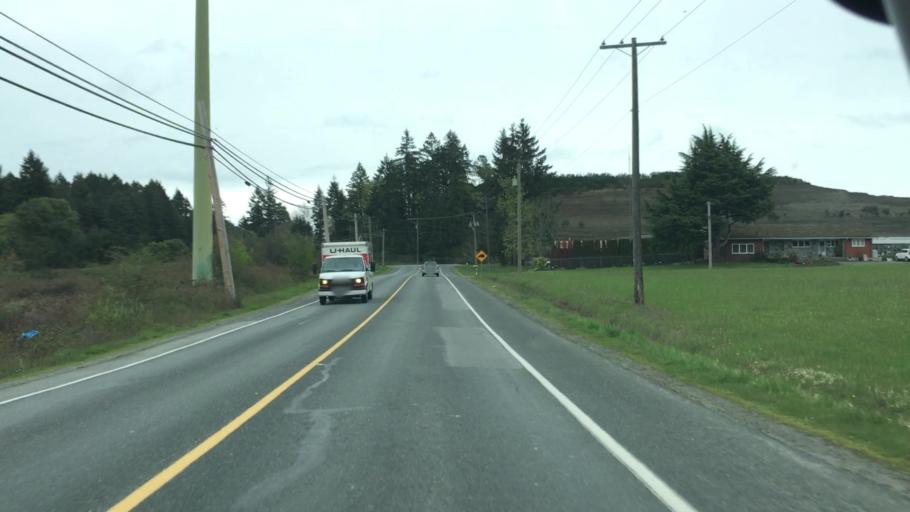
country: CA
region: British Columbia
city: North Saanich
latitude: 48.5651
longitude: -123.4311
